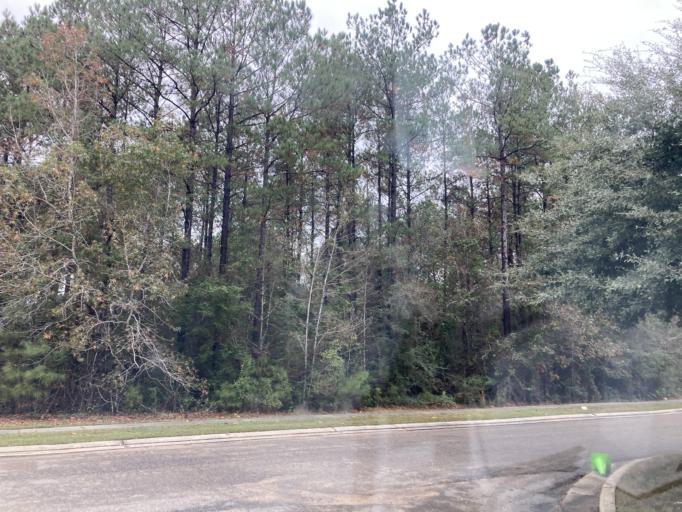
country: US
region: Mississippi
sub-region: Lamar County
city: West Hattiesburg
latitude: 31.2870
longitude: -89.4747
